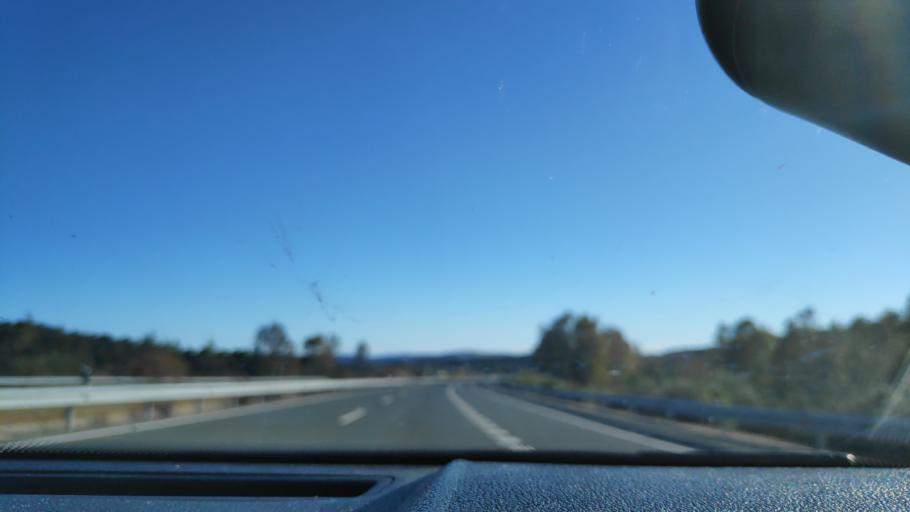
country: ES
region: Extremadura
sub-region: Provincia de Badajoz
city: Monesterio
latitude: 38.0355
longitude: -6.2240
